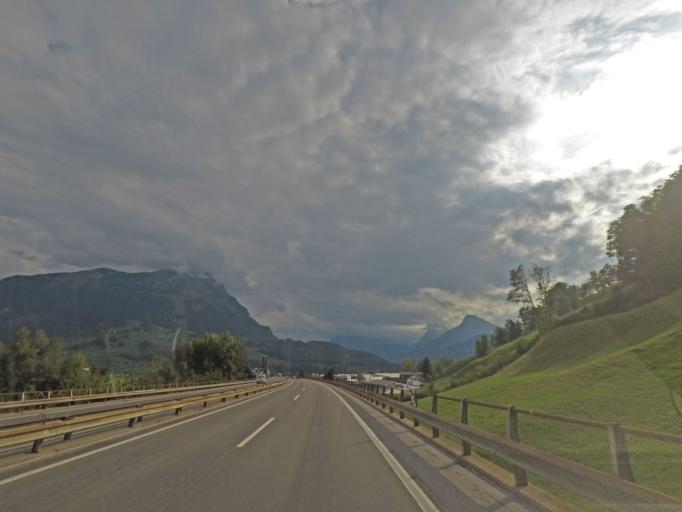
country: CH
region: Schwyz
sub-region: Bezirk Schwyz
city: Ingenbohl
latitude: 47.0186
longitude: 8.6264
